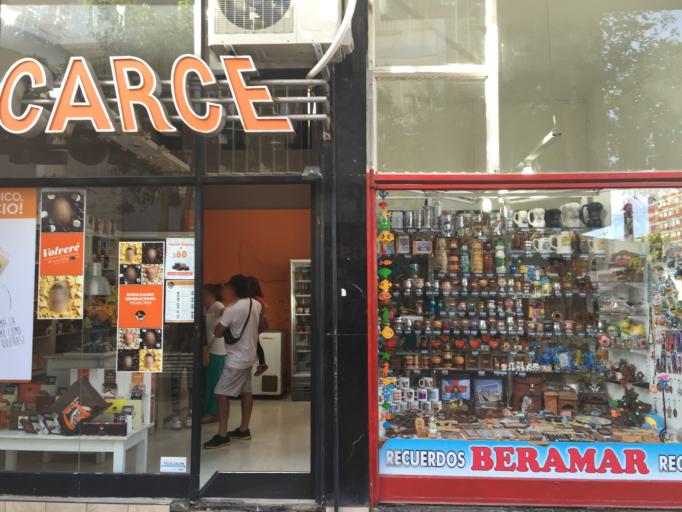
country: AR
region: Buenos Aires
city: Miramar
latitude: -38.2723
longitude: -57.8355
